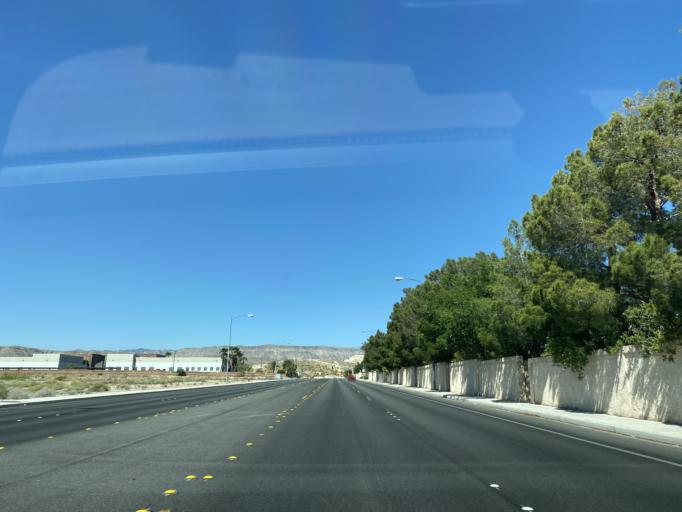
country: US
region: Nevada
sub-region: Clark County
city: Spring Valley
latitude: 36.0926
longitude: -115.2758
